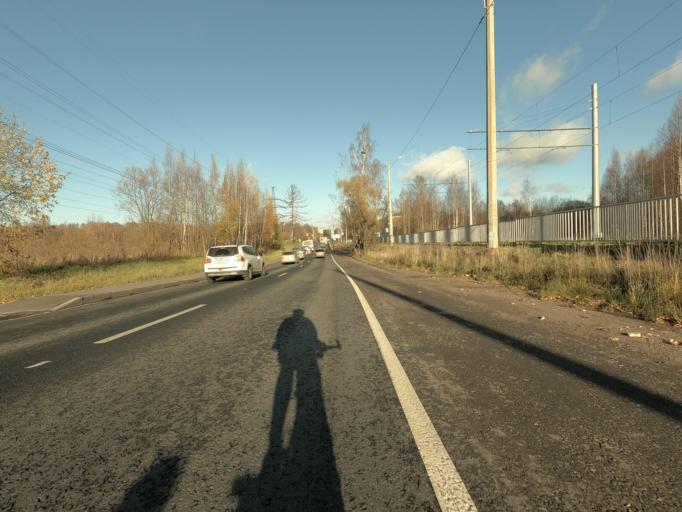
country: RU
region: St.-Petersburg
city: Krasnogvargeisky
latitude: 59.9677
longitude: 30.5025
